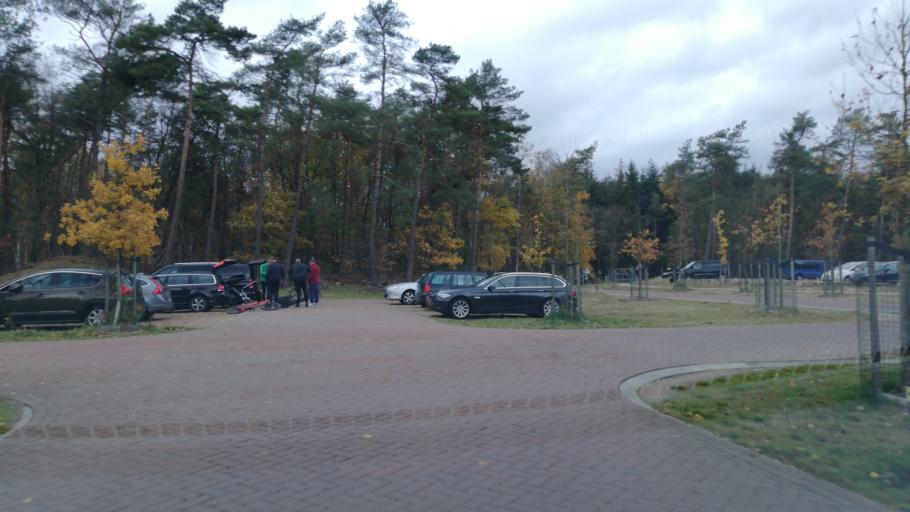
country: NL
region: Gelderland
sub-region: Gemeente Apeldoorn
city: Beekbergen
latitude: 52.1676
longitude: 5.9082
